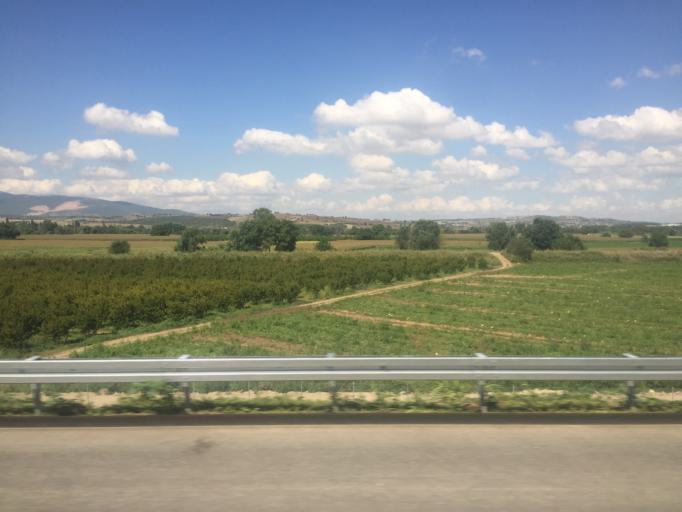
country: TR
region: Balikesir
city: Gobel
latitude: 40.0001
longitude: 28.1929
